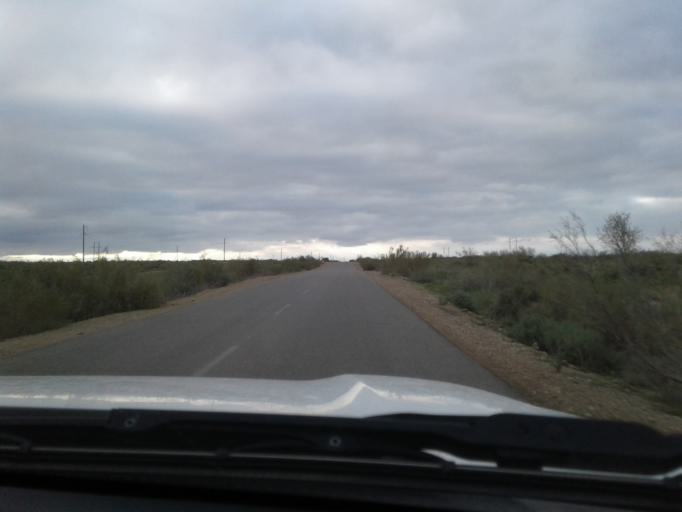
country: TM
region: Lebap
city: Sayat
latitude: 38.9185
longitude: 64.2963
